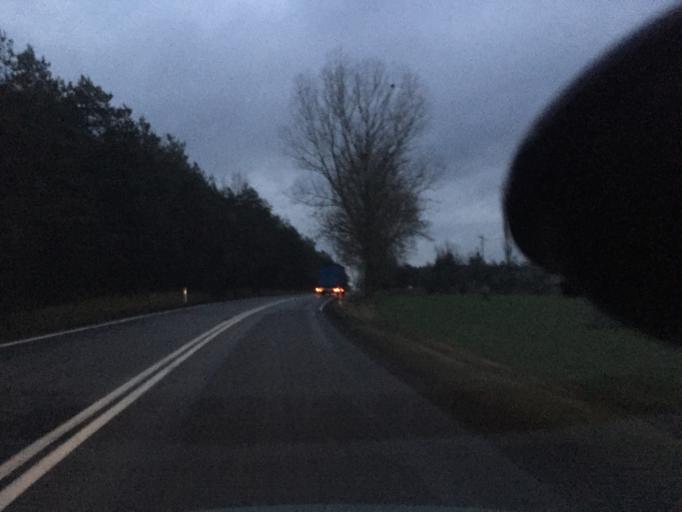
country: PL
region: Kujawsko-Pomorskie
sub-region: Powiat wabrzeski
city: Debowa Laka
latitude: 53.1917
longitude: 19.0654
